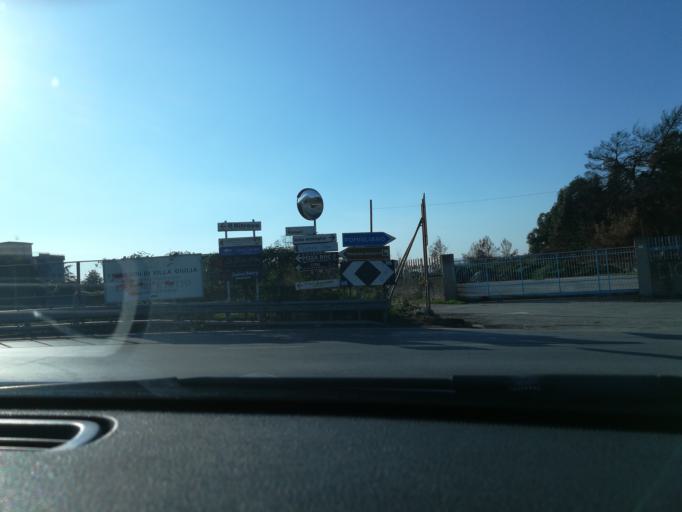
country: IT
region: Campania
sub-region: Provincia di Napoli
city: Sant'Anastasia
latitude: 40.8753
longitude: 14.3865
